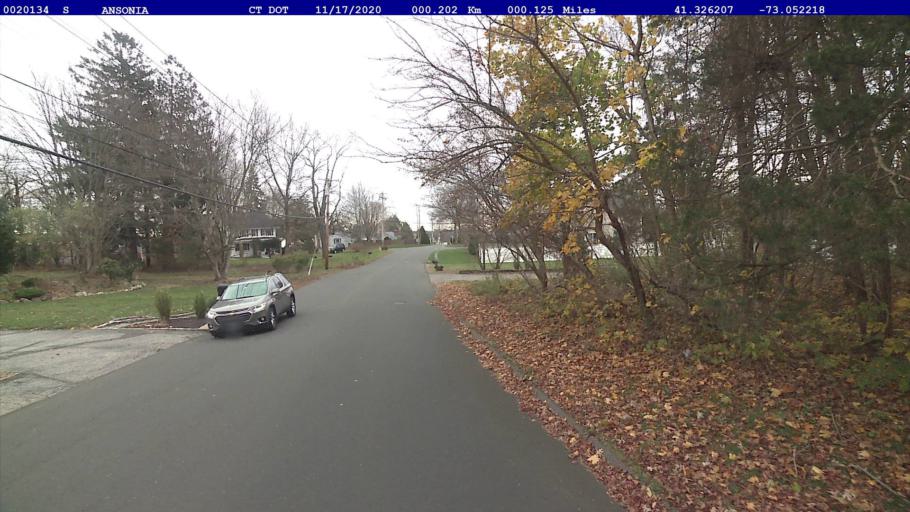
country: US
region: Connecticut
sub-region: New Haven County
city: Ansonia
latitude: 41.3262
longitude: -73.0523
